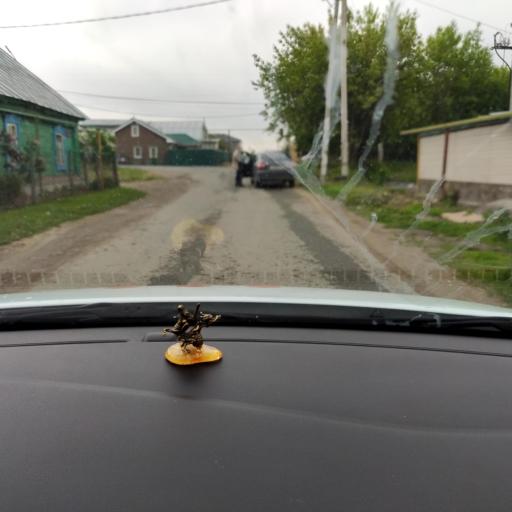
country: RU
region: Tatarstan
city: Verkhniy Uslon
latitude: 55.8002
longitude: 49.0326
